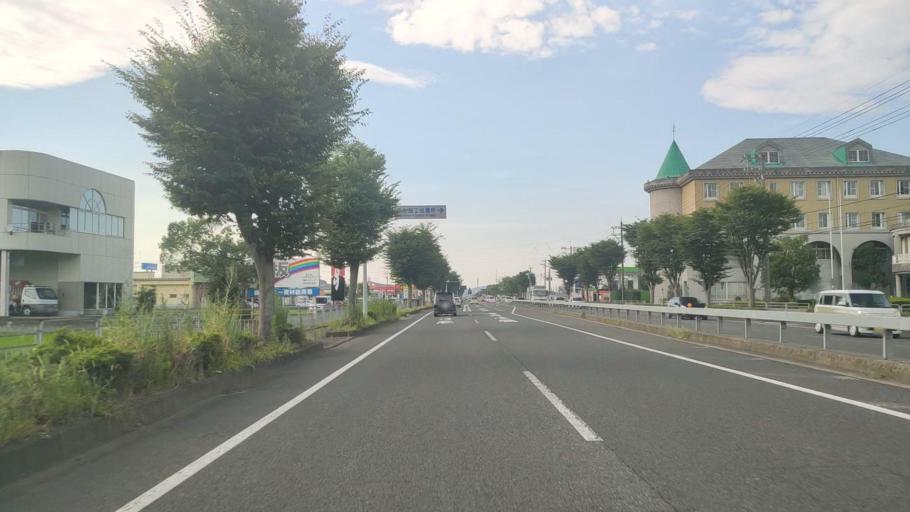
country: JP
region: Fukui
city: Takefu
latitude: 35.9154
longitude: 136.1913
